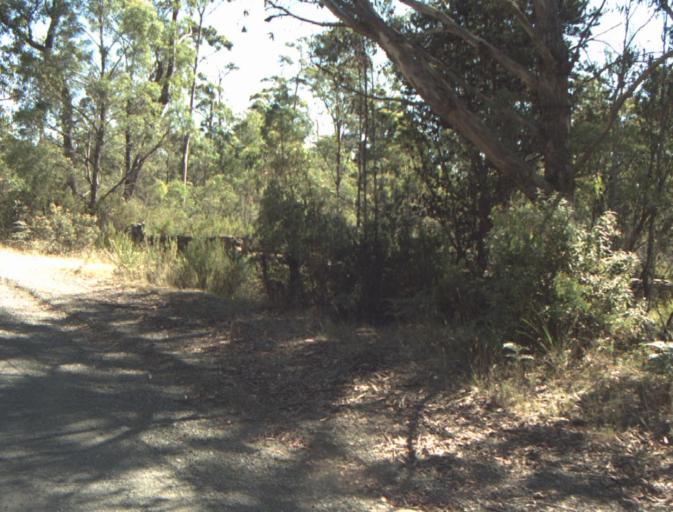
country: AU
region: Tasmania
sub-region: Launceston
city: Mayfield
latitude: -41.3393
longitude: 147.2092
